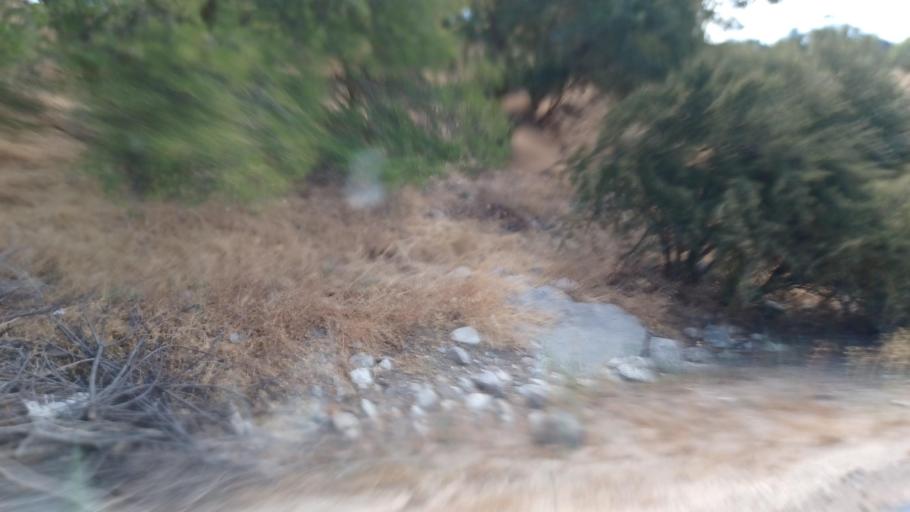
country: CY
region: Pafos
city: Mesogi
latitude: 34.8831
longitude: 32.6102
